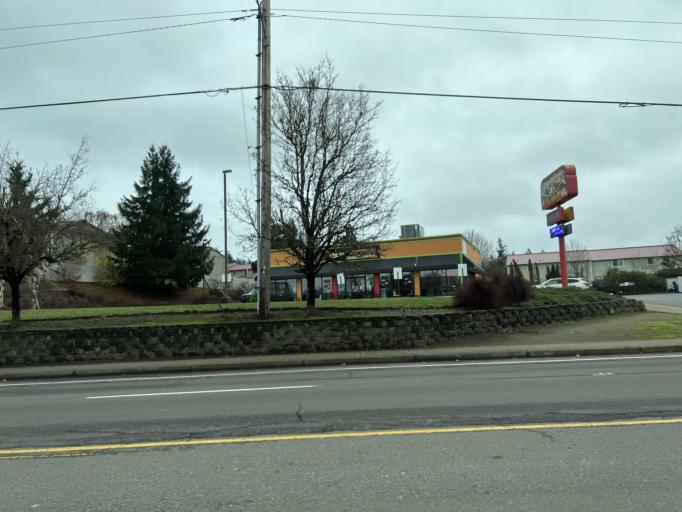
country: US
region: Oregon
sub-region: Marion County
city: Salem
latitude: 44.8845
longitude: -123.0318
